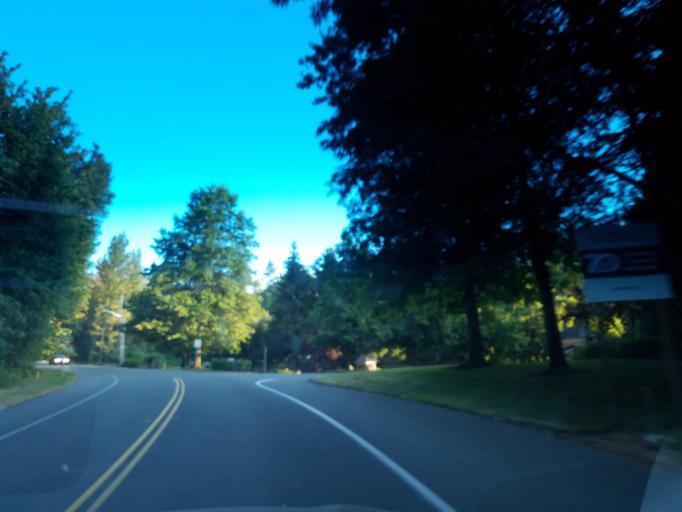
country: US
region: Washington
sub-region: King County
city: City of Sammamish
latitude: 47.6377
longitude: -122.0143
